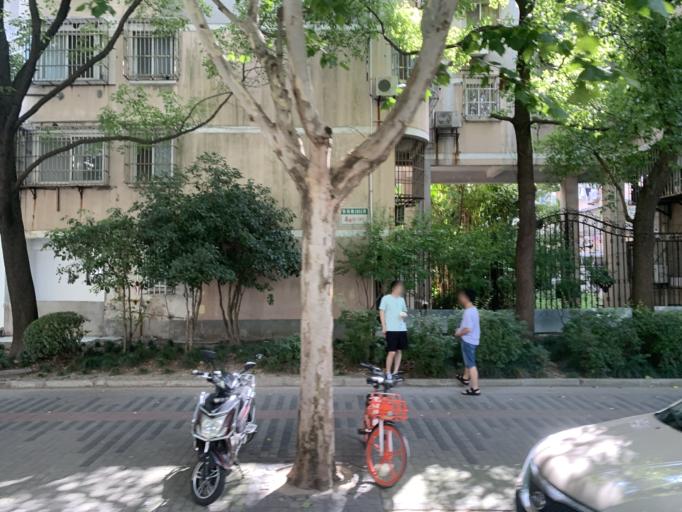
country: CN
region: Shanghai Shi
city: Pudong
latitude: 31.2488
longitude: 121.5599
